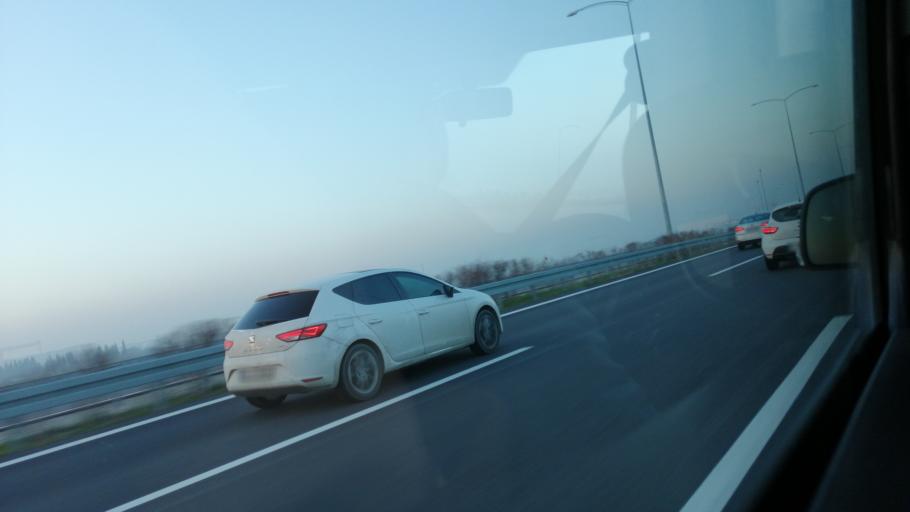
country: TR
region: Yalova
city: Altinova
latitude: 40.7123
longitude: 29.4978
